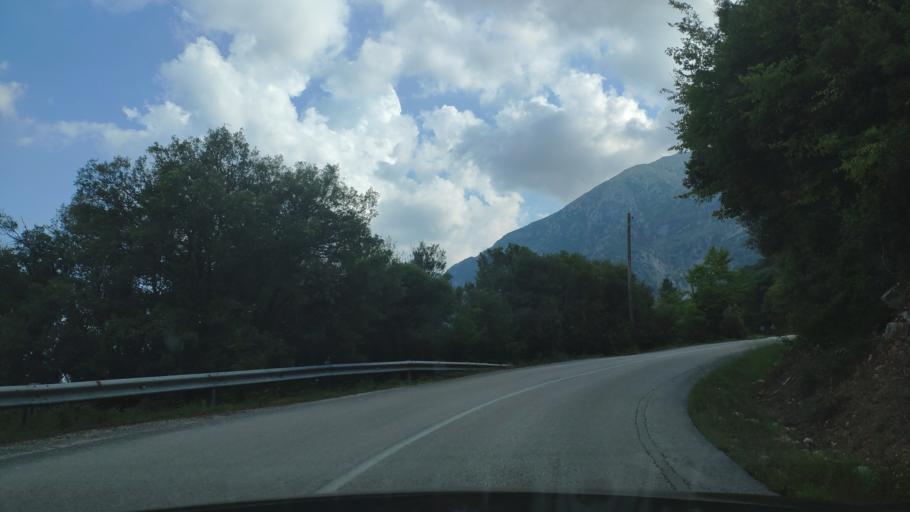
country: GR
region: Epirus
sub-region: Nomos Artas
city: Agios Dimitrios
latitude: 39.4547
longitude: 21.0235
